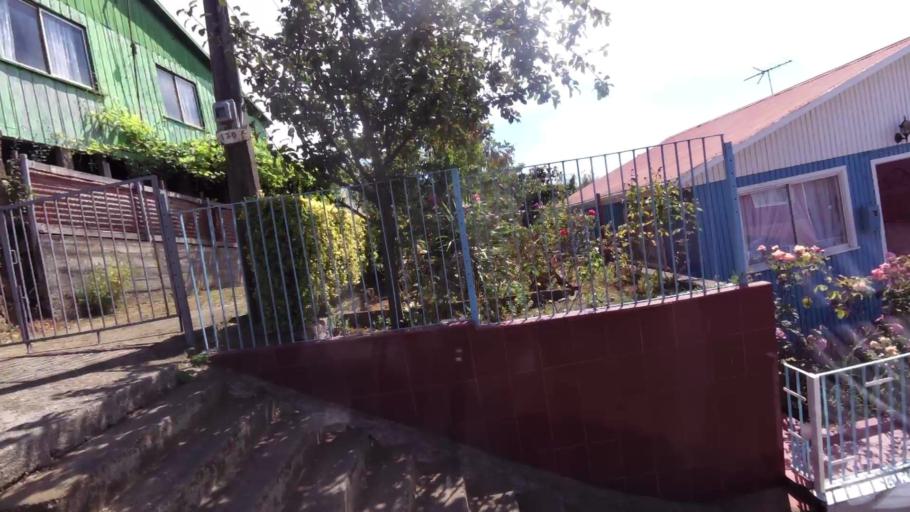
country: CL
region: Biobio
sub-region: Provincia de Concepcion
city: Talcahuano
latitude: -36.7090
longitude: -73.1187
